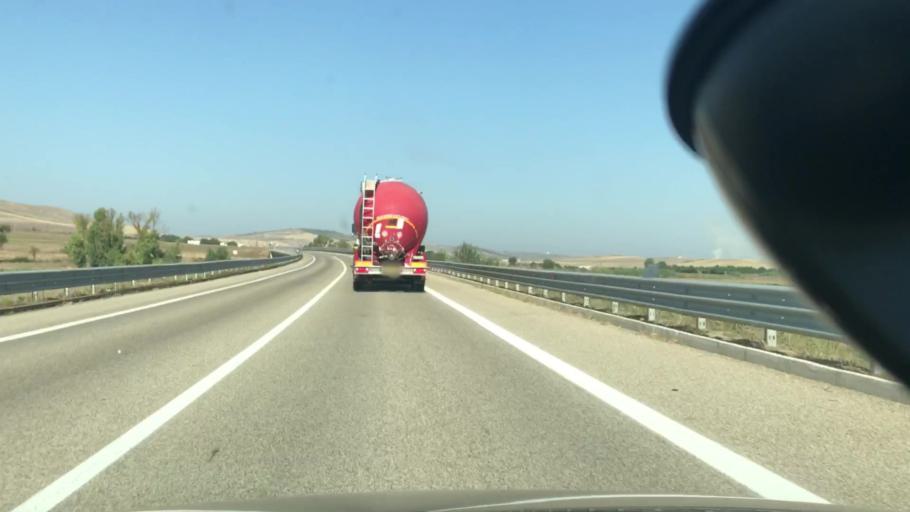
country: IT
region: Basilicate
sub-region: Provincia di Matera
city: Irsina
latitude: 40.7813
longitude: 16.3120
